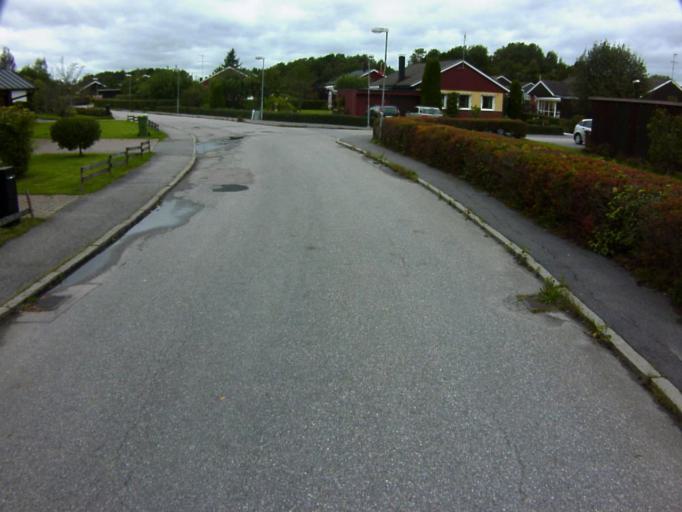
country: SE
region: Soedermanland
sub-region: Eskilstuna Kommun
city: Torshalla
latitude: 59.3799
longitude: 16.4720
